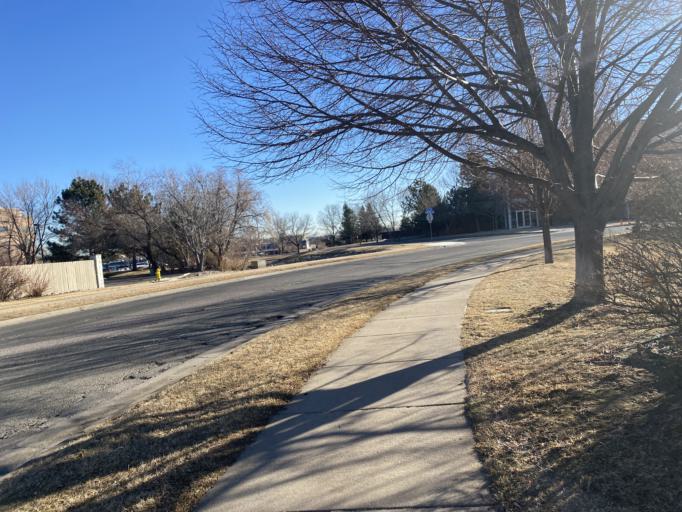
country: US
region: Colorado
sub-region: Jefferson County
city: Arvada
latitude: 39.8109
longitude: -105.1398
